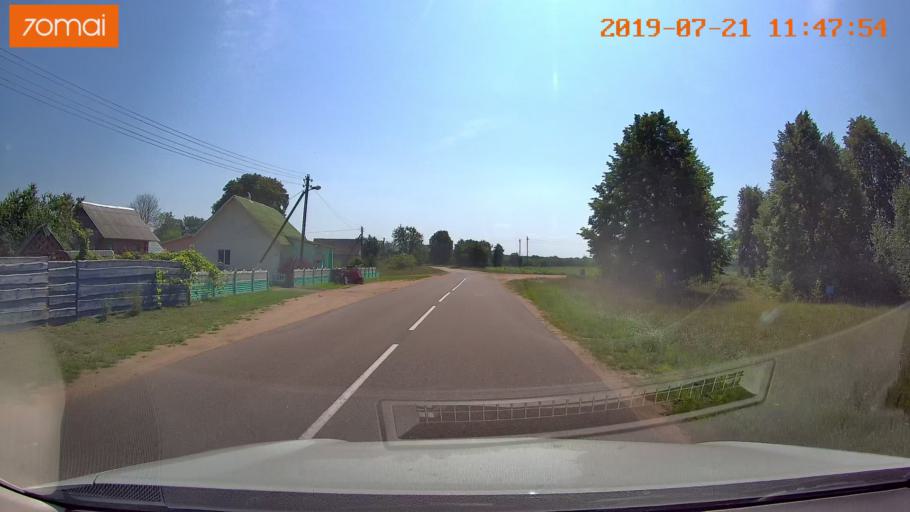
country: BY
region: Grodnenskaya
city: Lyubcha
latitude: 53.9006
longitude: 26.0547
